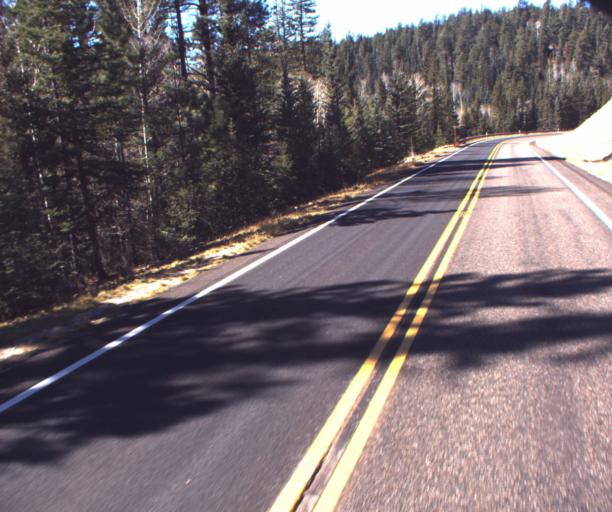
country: US
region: Arizona
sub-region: Coconino County
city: Grand Canyon
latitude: 36.5146
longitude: -112.1393
